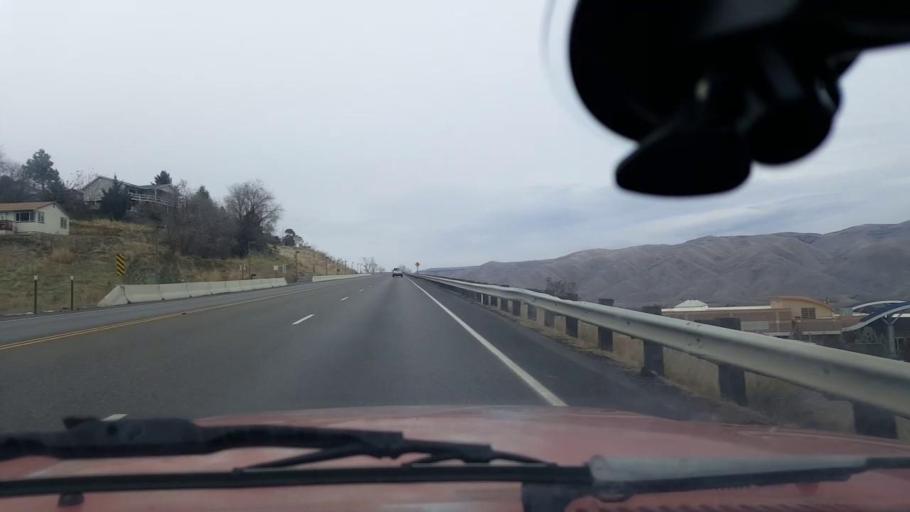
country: US
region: Washington
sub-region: Asotin County
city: West Clarkston-Highland
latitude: 46.3993
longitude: -117.0715
